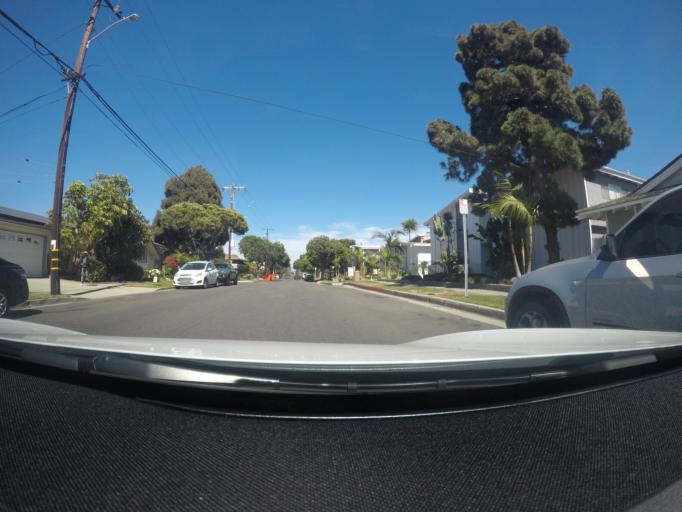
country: US
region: California
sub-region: Los Angeles County
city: Torrance
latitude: 33.8413
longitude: -118.3571
